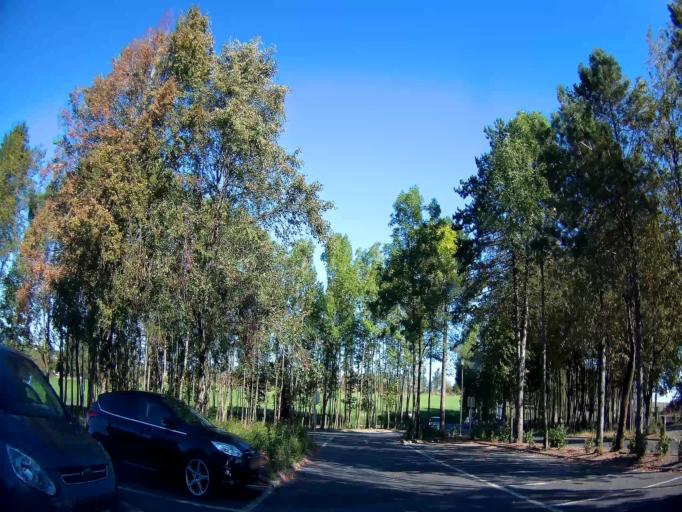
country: BE
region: Wallonia
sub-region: Province du Luxembourg
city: Bastogne
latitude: 50.0112
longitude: 5.7399
